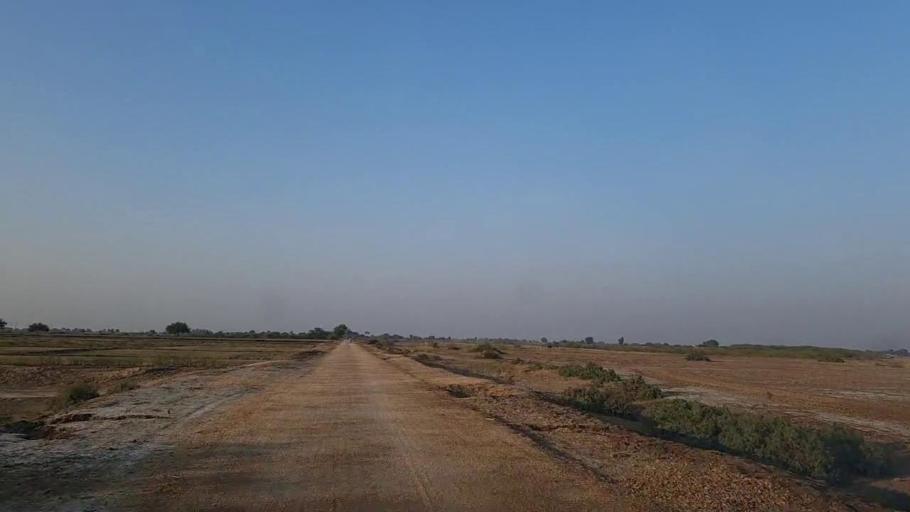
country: PK
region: Sindh
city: Naukot
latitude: 24.9620
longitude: 69.4562
